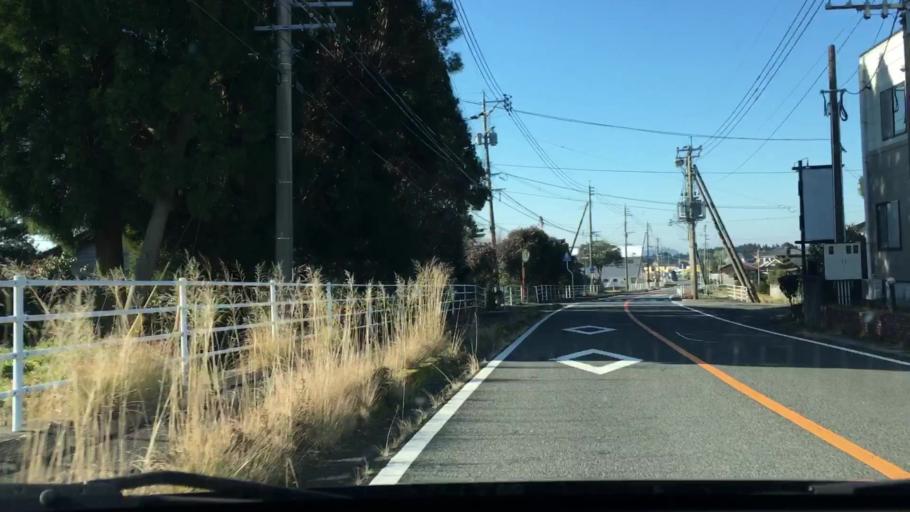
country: JP
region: Kagoshima
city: Kajiki
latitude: 31.7880
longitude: 130.7098
